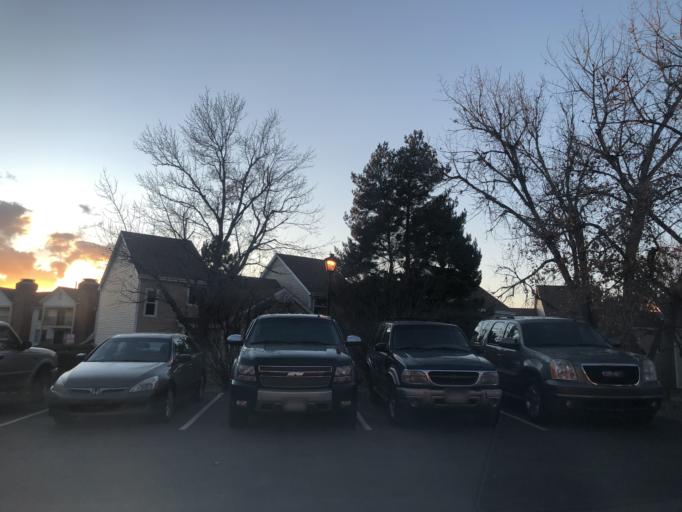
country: US
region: Colorado
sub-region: Adams County
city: Aurora
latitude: 39.7097
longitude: -104.8009
